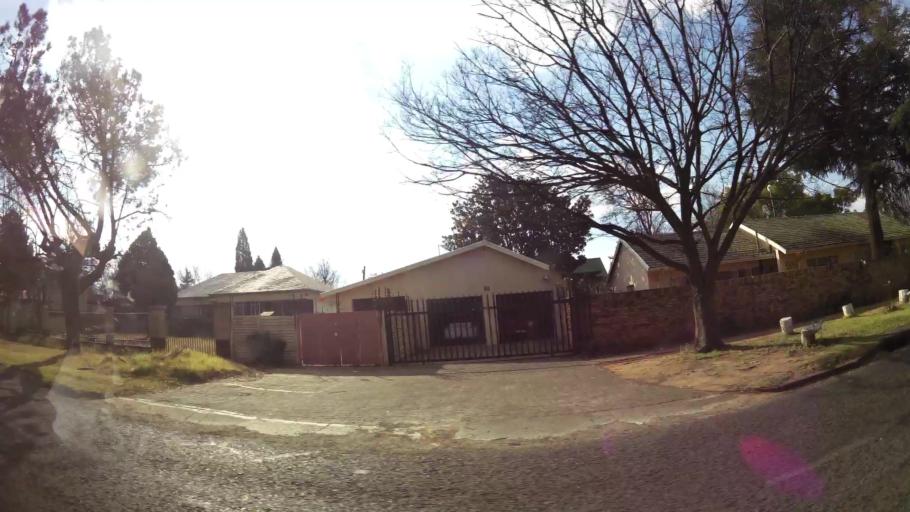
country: ZA
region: Gauteng
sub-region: West Rand District Municipality
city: Krugersdorp
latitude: -26.0871
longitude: 27.7751
